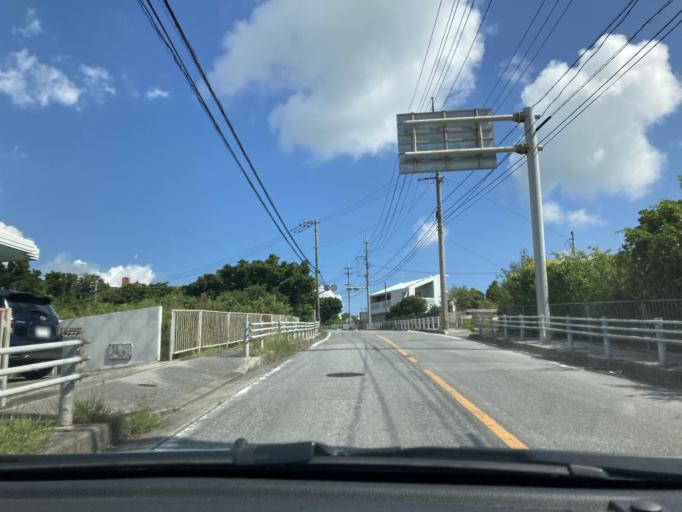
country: JP
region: Okinawa
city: Tomigusuku
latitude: 26.1439
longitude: 127.7920
